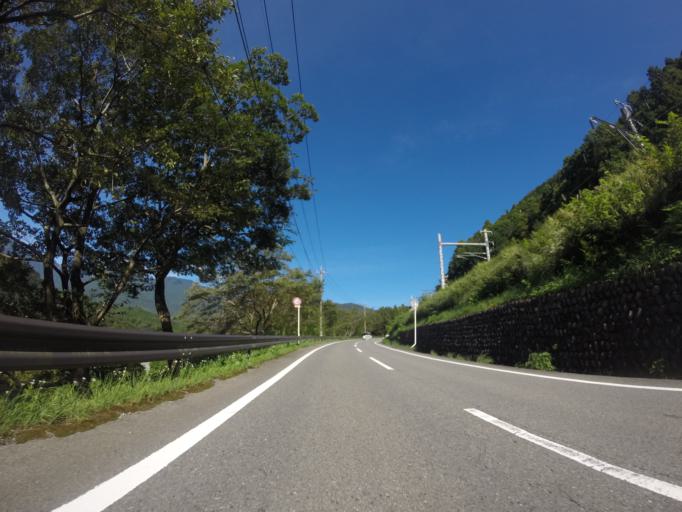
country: JP
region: Shizuoka
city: Fujinomiya
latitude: 35.2937
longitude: 138.4583
